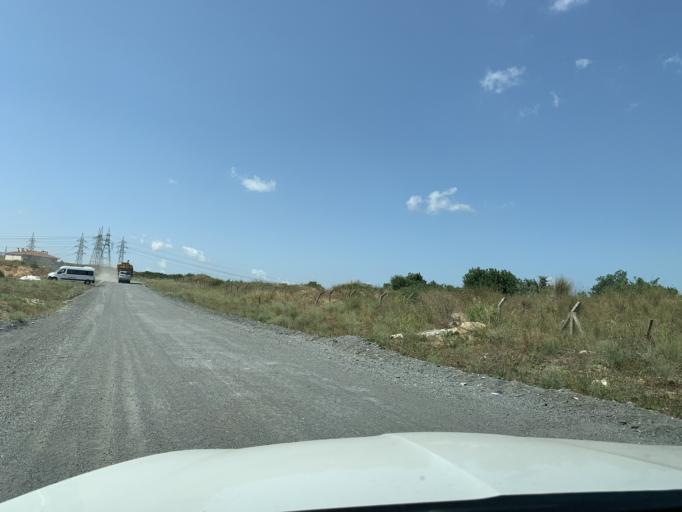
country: TR
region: Istanbul
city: Esenyurt
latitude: 41.0856
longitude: 28.6933
